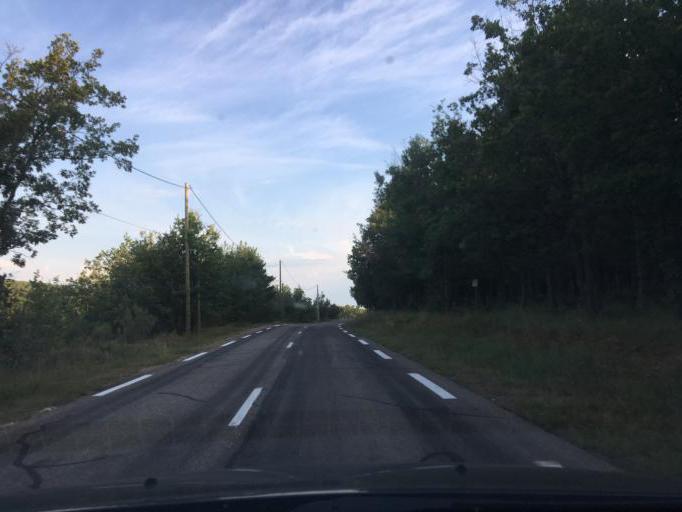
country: FR
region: Provence-Alpes-Cote d'Azur
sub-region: Departement du Var
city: Aups
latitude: 43.6921
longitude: 6.2200
